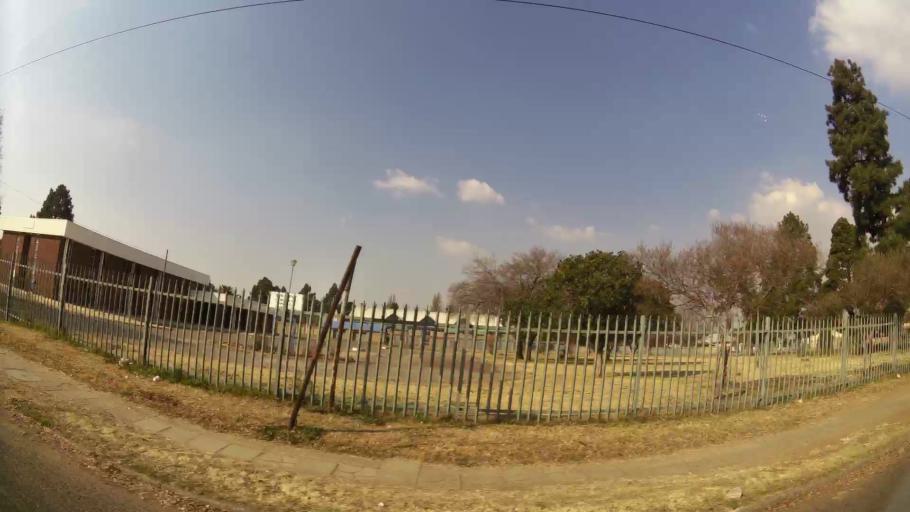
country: ZA
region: Gauteng
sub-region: Ekurhuleni Metropolitan Municipality
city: Boksburg
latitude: -26.2066
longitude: 28.2538
